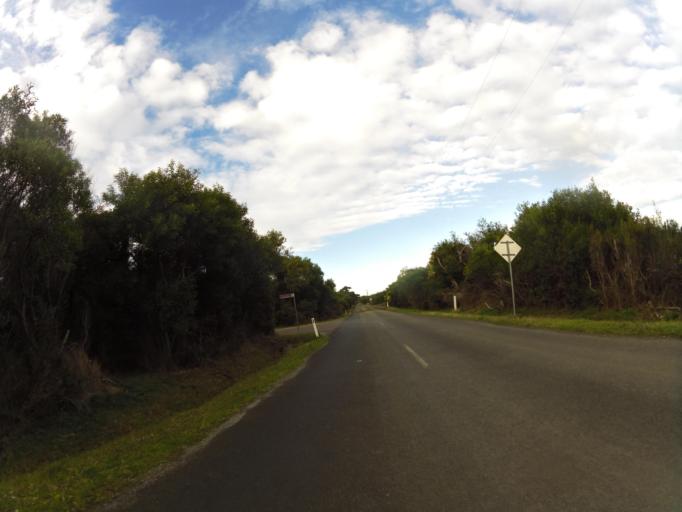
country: AU
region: Victoria
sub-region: Bass Coast
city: North Wonthaggi
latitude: -38.6114
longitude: 145.5674
